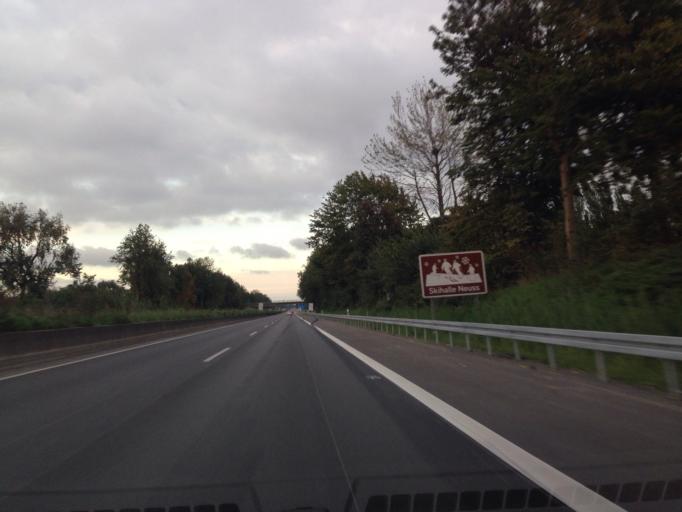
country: DE
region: North Rhine-Westphalia
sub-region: Regierungsbezirk Dusseldorf
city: Neubrueck
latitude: 51.1511
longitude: 6.6311
